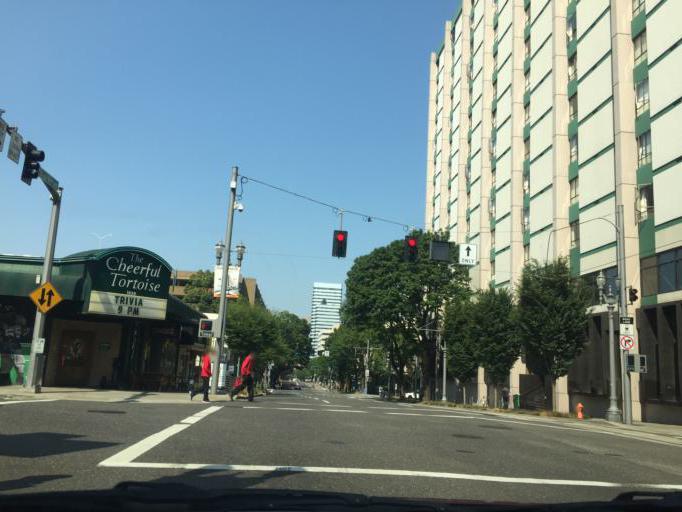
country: US
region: Oregon
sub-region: Multnomah County
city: Portland
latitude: 45.5097
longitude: -122.6837
